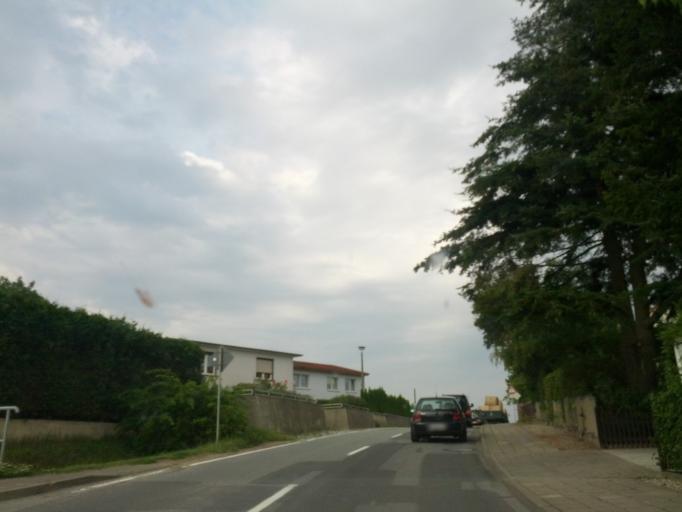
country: DE
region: Mecklenburg-Vorpommern
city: Kropelin
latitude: 54.0694
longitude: 11.8018
